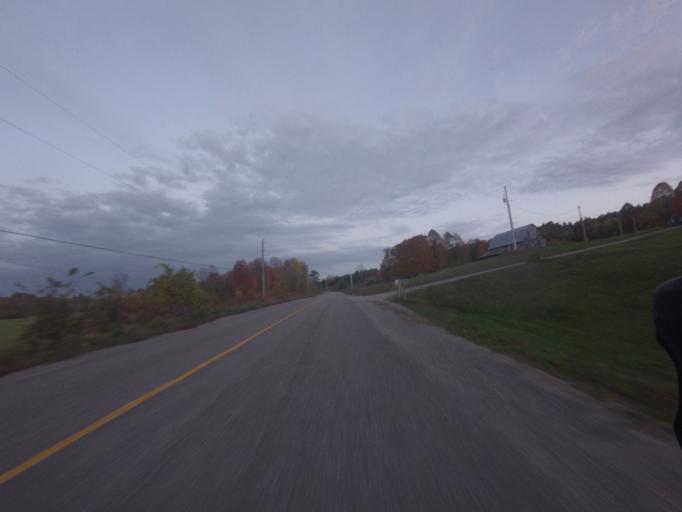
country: CA
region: Ontario
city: Renfrew
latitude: 45.3461
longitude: -76.9357
